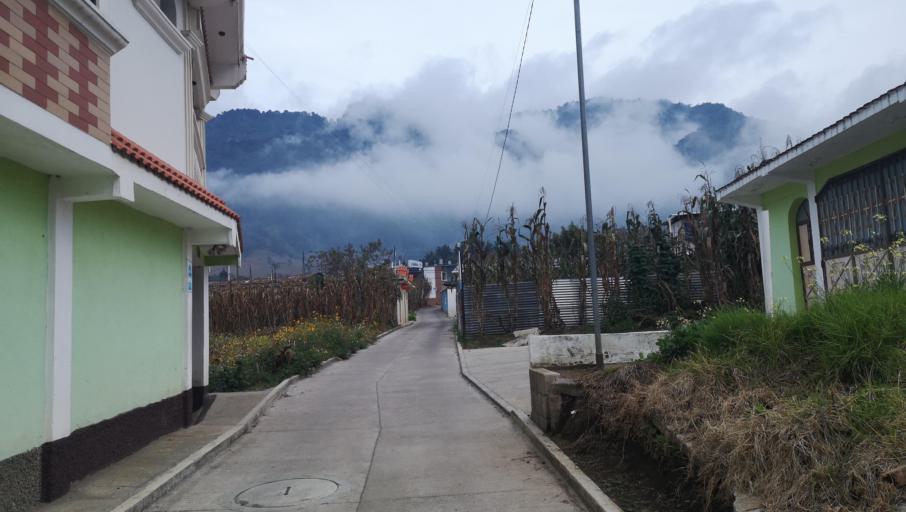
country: GT
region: Quetzaltenango
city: Cantel
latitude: 14.8182
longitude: -91.4360
